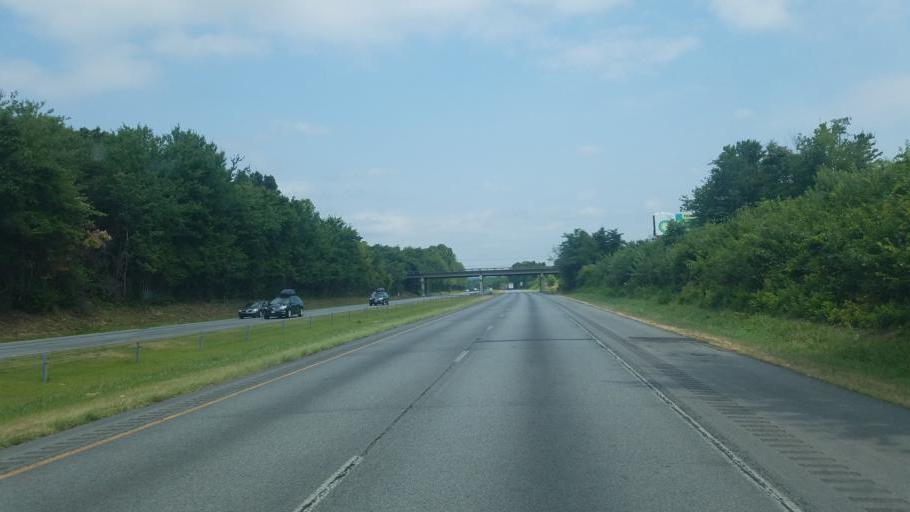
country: US
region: North Carolina
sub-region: Yadkin County
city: Jonesville
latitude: 36.2134
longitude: -80.8108
